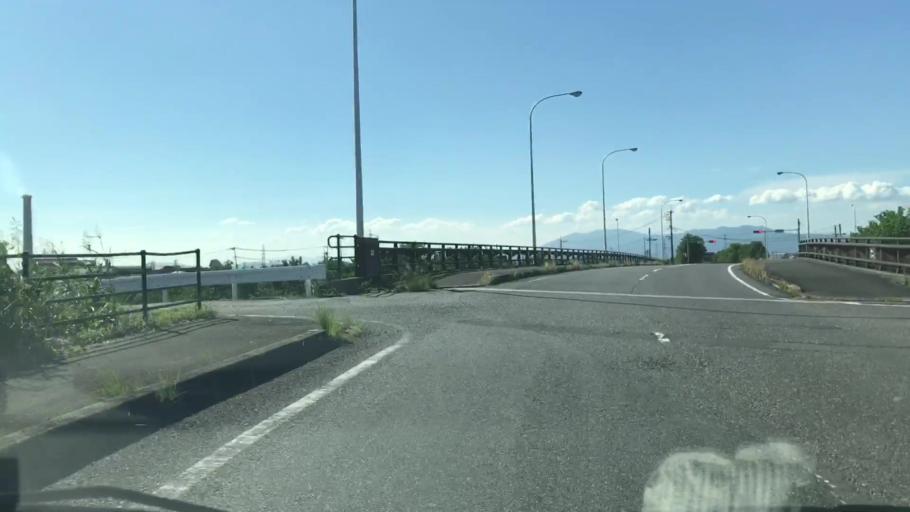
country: JP
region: Saga Prefecture
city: Okawa
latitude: 33.2279
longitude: 130.3709
